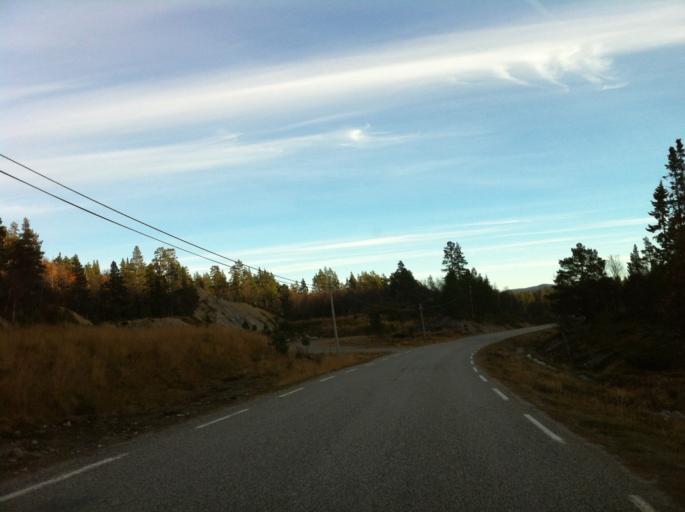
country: NO
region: Hedmark
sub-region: Engerdal
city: Engerdal
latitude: 62.0940
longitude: 12.0366
